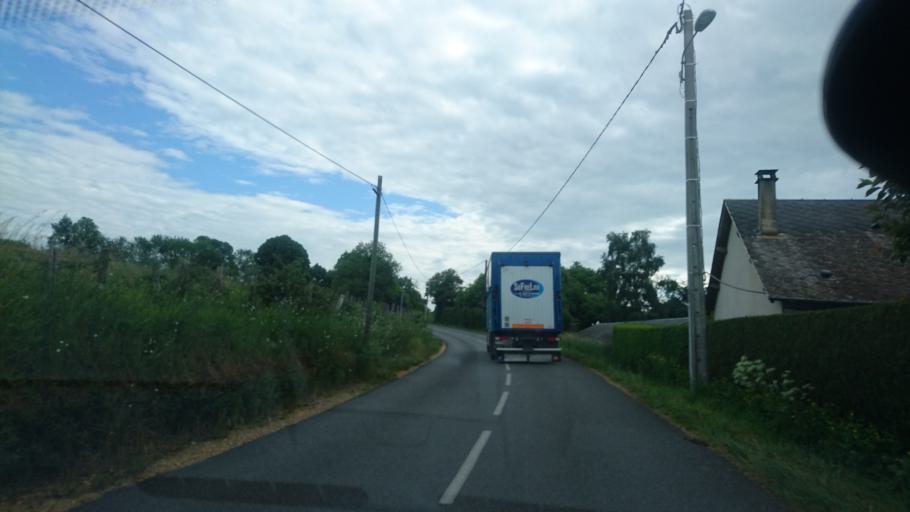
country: FR
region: Limousin
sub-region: Departement de la Haute-Vienne
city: Chateauneuf-la-Foret
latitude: 45.6836
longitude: 1.5844
